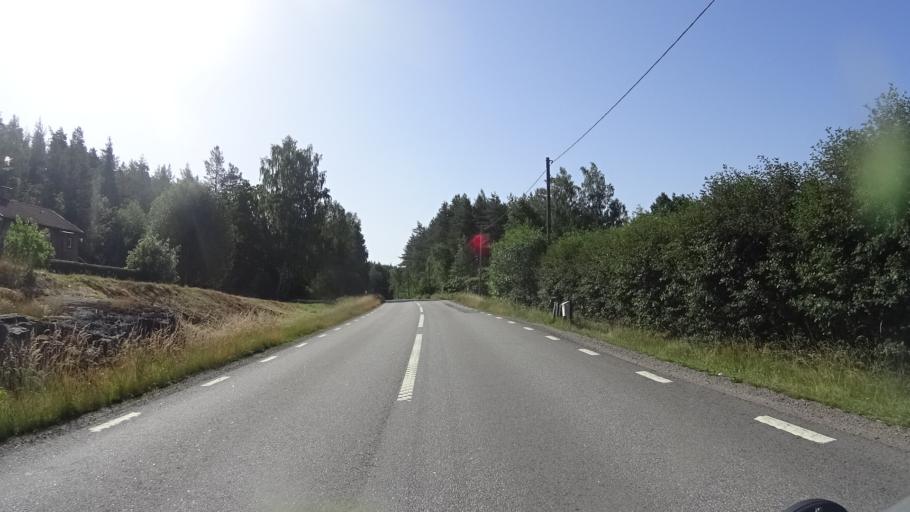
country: SE
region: OEstergoetland
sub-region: Atvidabergs Kommun
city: Atvidaberg
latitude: 58.1048
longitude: 16.1129
